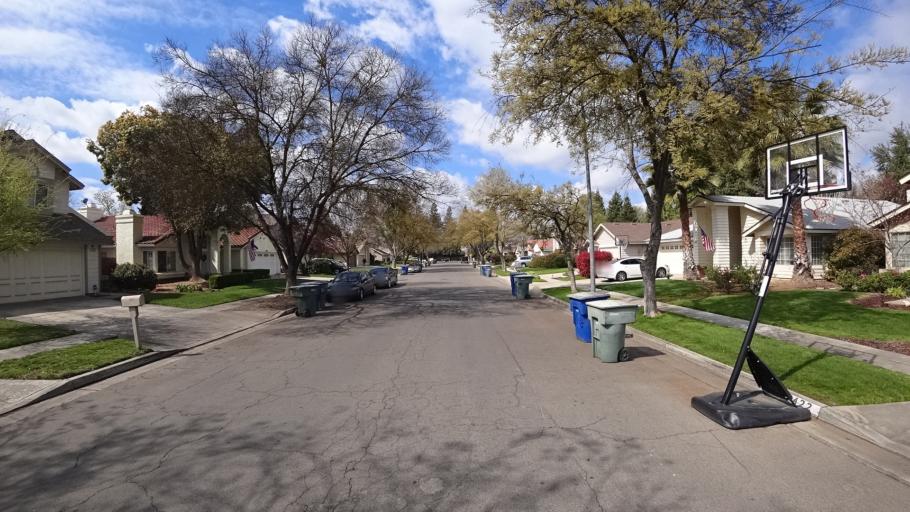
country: US
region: California
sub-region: Fresno County
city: Fresno
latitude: 36.8408
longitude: -119.8549
